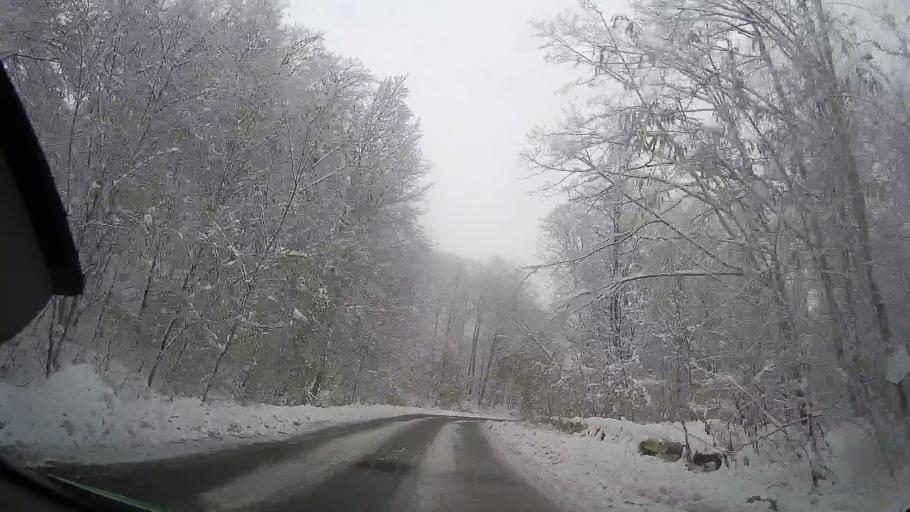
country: RO
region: Neamt
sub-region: Comuna Valea Ursului
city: Valea Ursului
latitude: 46.8414
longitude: 27.0685
